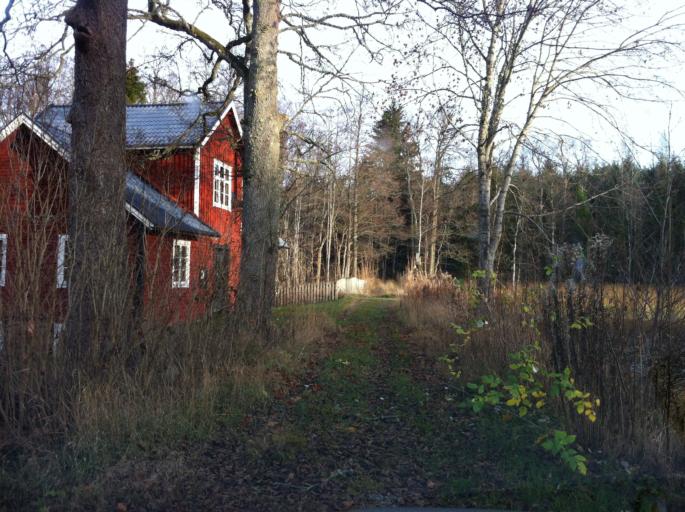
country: SE
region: Joenkoeping
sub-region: Eksjo Kommun
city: Mariannelund
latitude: 57.4771
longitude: 15.6561
